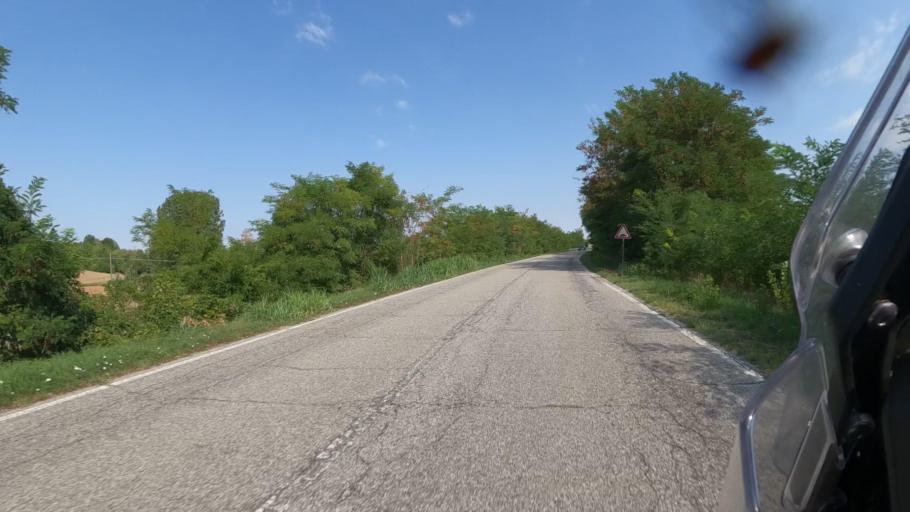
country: IT
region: Piedmont
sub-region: Provincia di Alessandria
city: Quattordio
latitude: 44.9060
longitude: 8.4012
